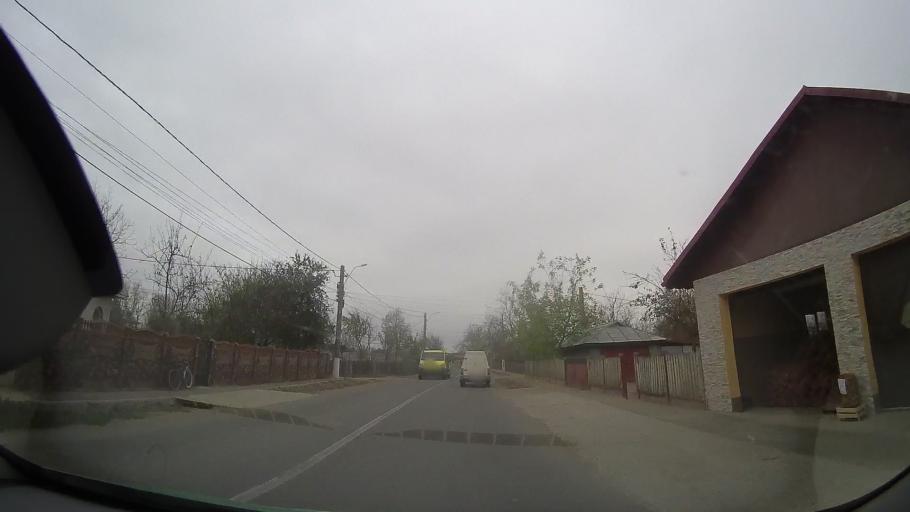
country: RO
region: Braila
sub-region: Comuna Budesti
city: Tataru
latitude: 44.8497
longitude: 27.4276
